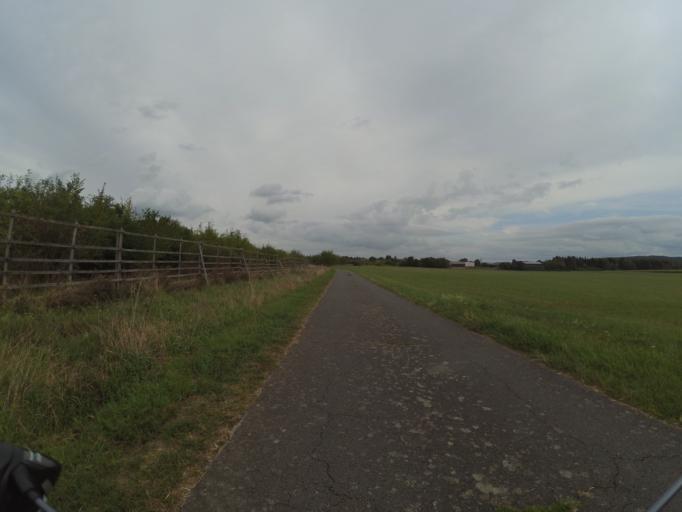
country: DE
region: Rheinland-Pfalz
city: Herforst
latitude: 49.9633
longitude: 6.6922
